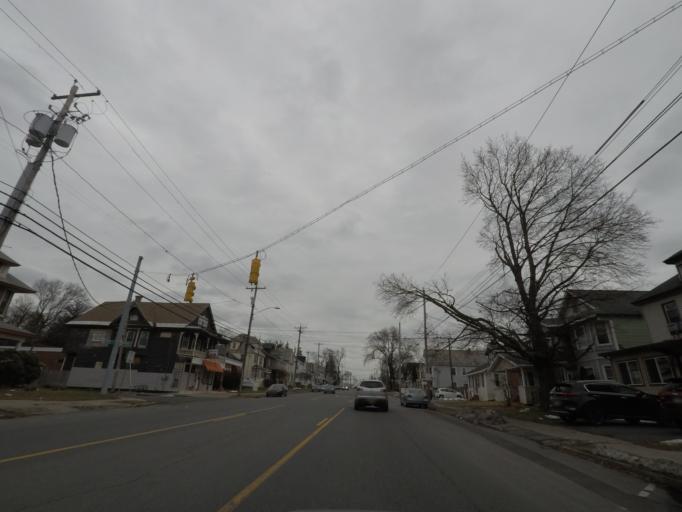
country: US
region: New York
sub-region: Schenectady County
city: Schenectady
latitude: 42.7907
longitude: -73.9157
